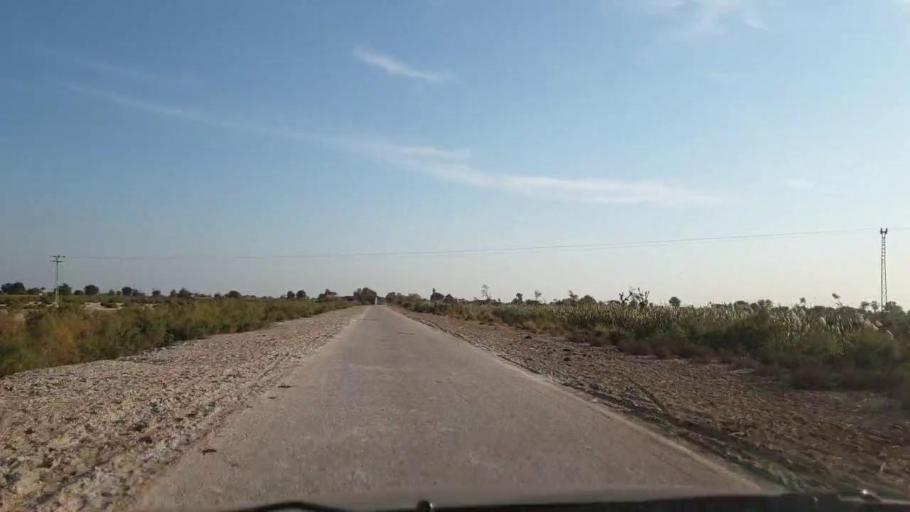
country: PK
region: Sindh
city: Khadro
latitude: 26.2054
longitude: 68.7467
